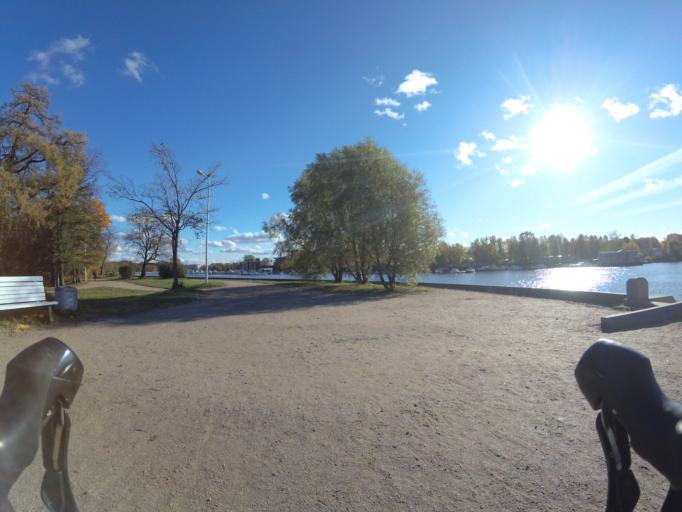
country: RU
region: St.-Petersburg
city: Staraya Derevnya
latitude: 59.9800
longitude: 30.2367
